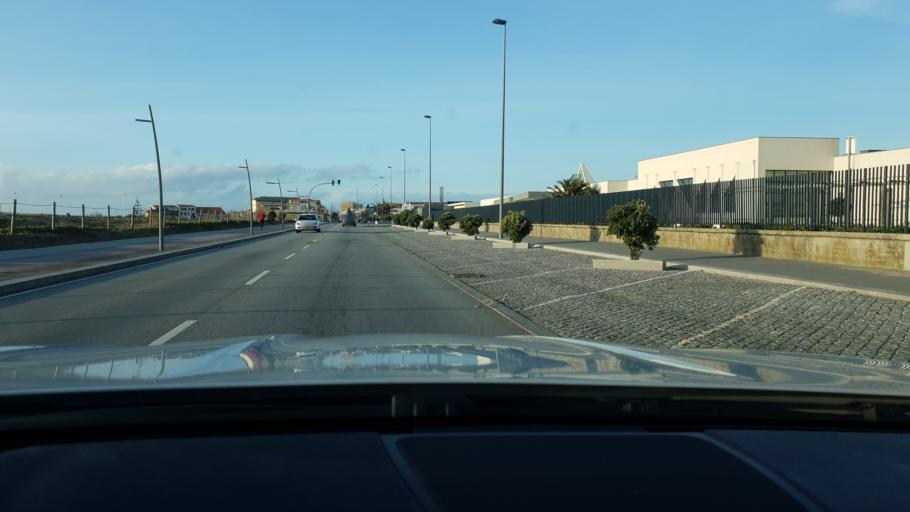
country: PT
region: Porto
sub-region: Matosinhos
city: Lavra
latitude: 41.2327
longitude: -8.7201
